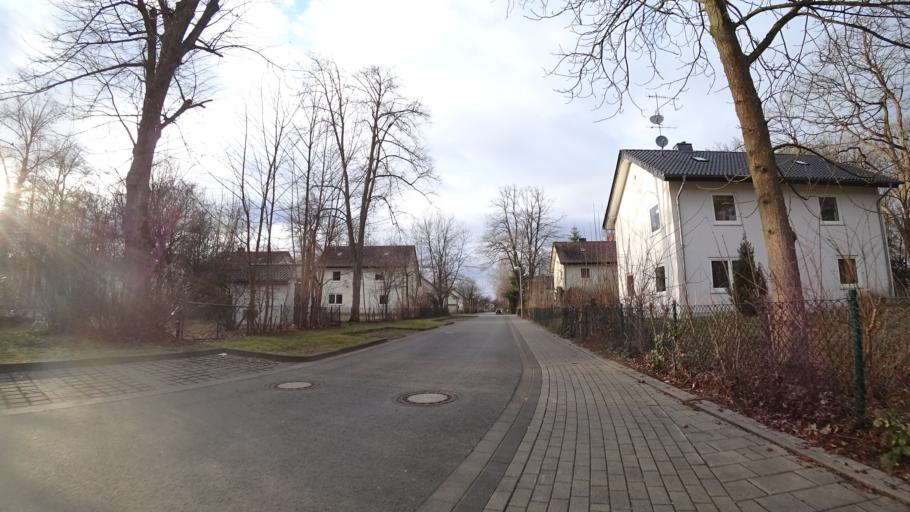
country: DE
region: North Rhine-Westphalia
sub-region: Regierungsbezirk Detmold
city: Guetersloh
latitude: 51.9011
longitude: 8.3964
